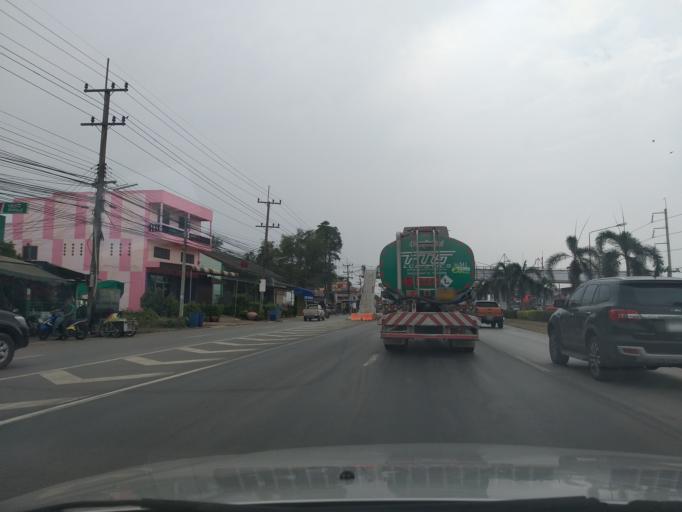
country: TH
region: Rayong
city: Klaeng
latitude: 12.7809
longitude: 101.7343
